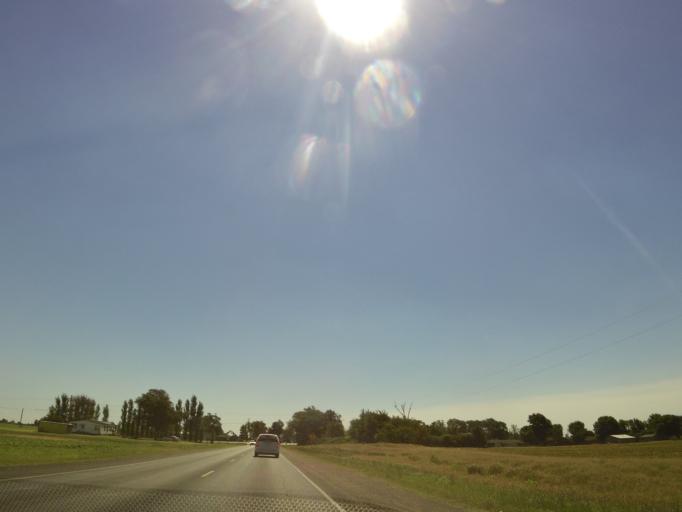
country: US
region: Missouri
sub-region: Dunklin County
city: Clarkton
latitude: 36.4983
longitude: -89.9742
